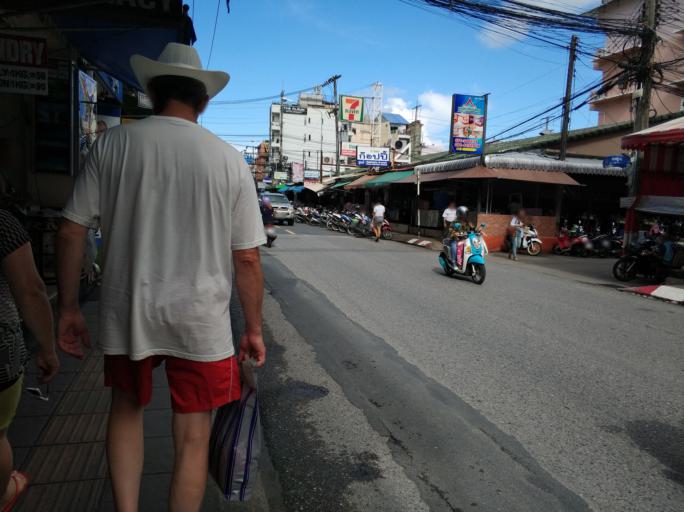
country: TH
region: Phuket
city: Patong
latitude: 7.8971
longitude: 98.3004
